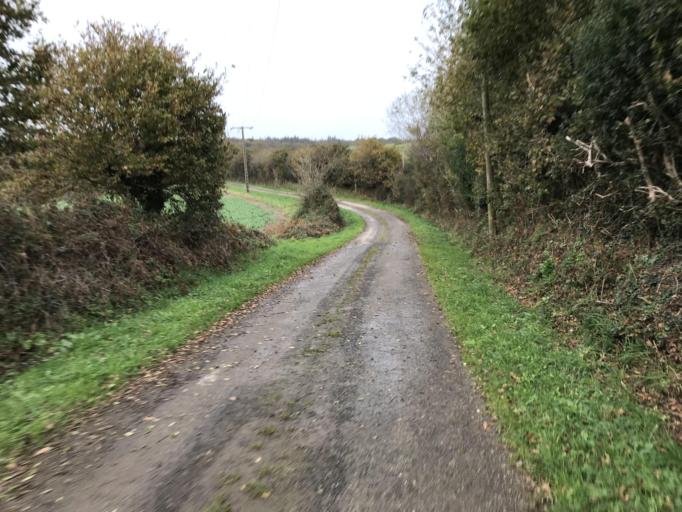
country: FR
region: Brittany
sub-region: Departement du Finistere
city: Hopital-Camfrout
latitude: 48.3233
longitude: -4.2144
